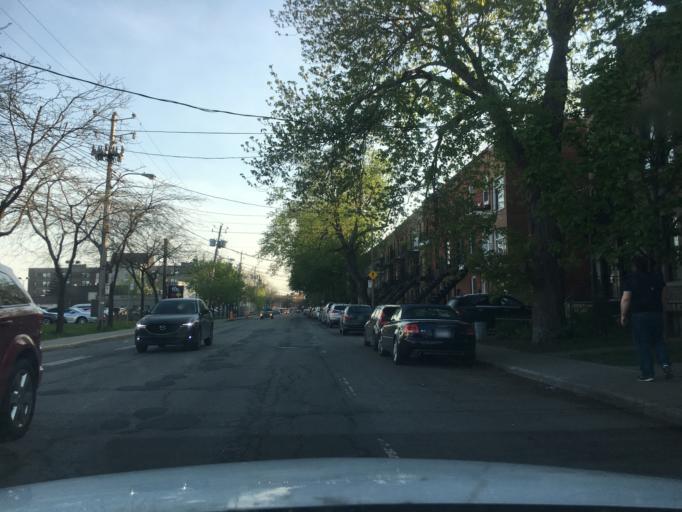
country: CA
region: Quebec
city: Westmount
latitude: 45.4706
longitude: -73.5643
